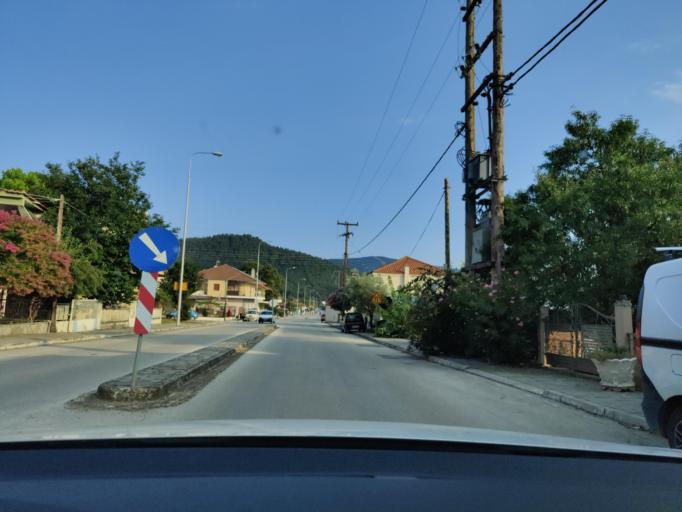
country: GR
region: East Macedonia and Thrace
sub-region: Nomos Kavalas
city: Zygos
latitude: 41.0154
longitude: 24.3800
